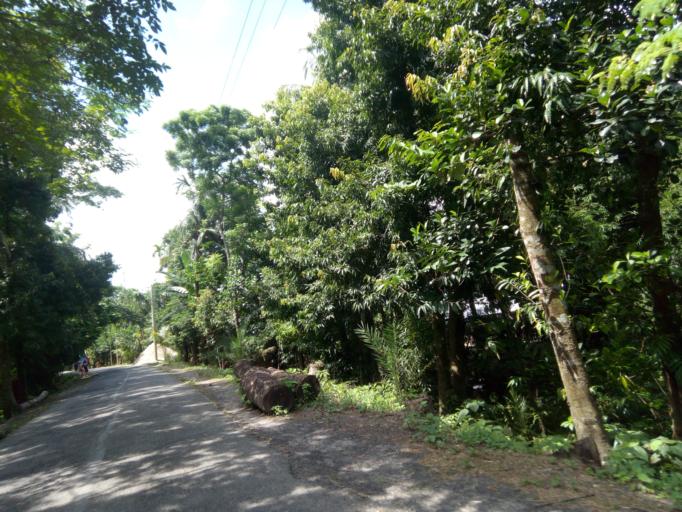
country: BD
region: Khulna
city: Kalia
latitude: 23.0165
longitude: 89.7180
